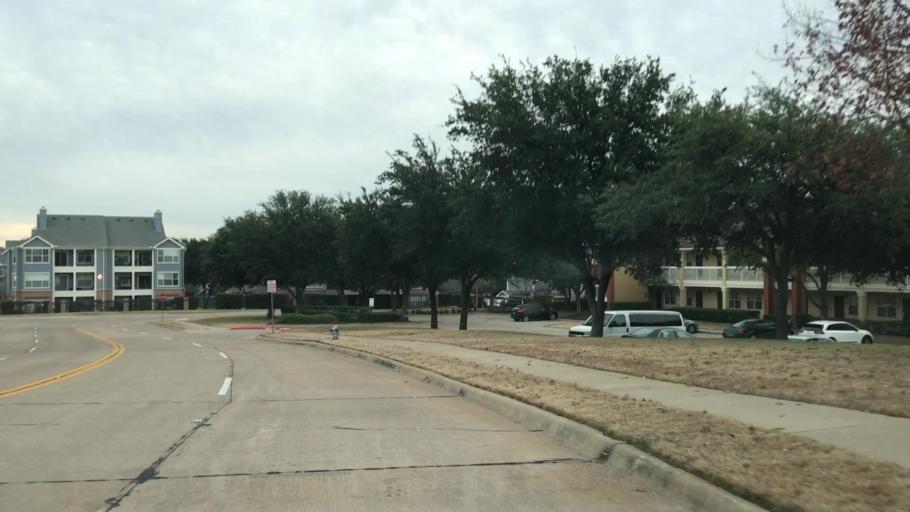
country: US
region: Texas
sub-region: Dallas County
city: Irving
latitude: 32.8824
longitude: -96.9623
